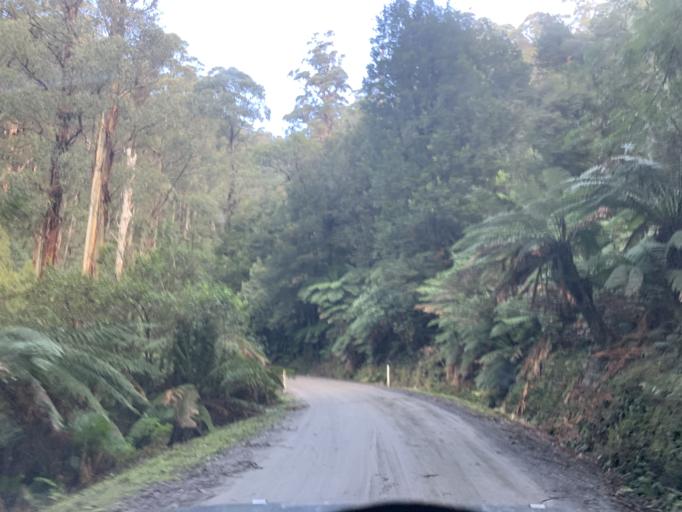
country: AU
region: Victoria
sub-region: Yarra Ranges
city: Millgrove
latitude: -37.6990
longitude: 145.7210
